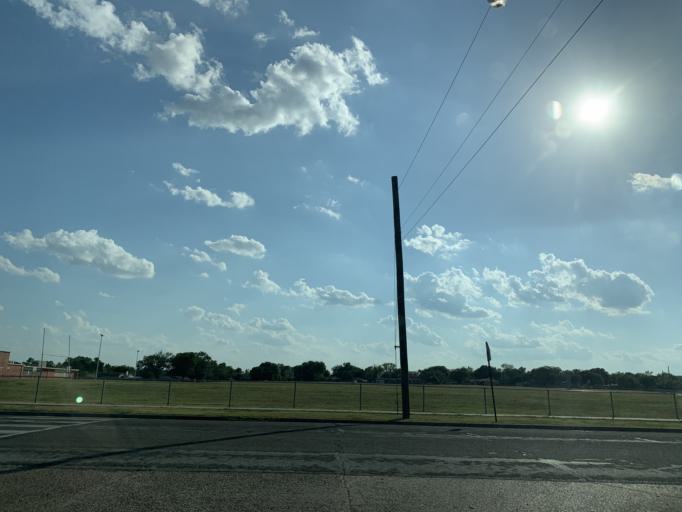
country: US
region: Texas
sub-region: Dallas County
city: Hutchins
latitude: 32.6926
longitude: -96.7814
